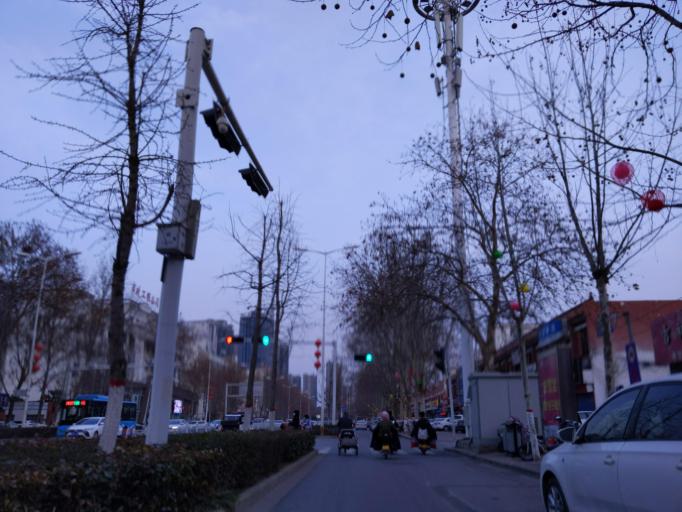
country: CN
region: Henan Sheng
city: Zhongyuanlu
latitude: 35.7804
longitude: 115.0387
